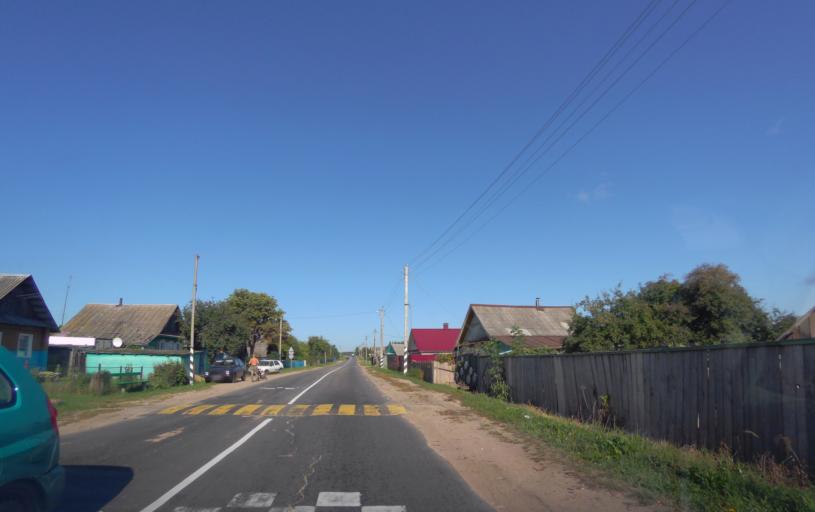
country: BY
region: Minsk
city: Horad Barysaw
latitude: 54.2590
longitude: 28.3835
